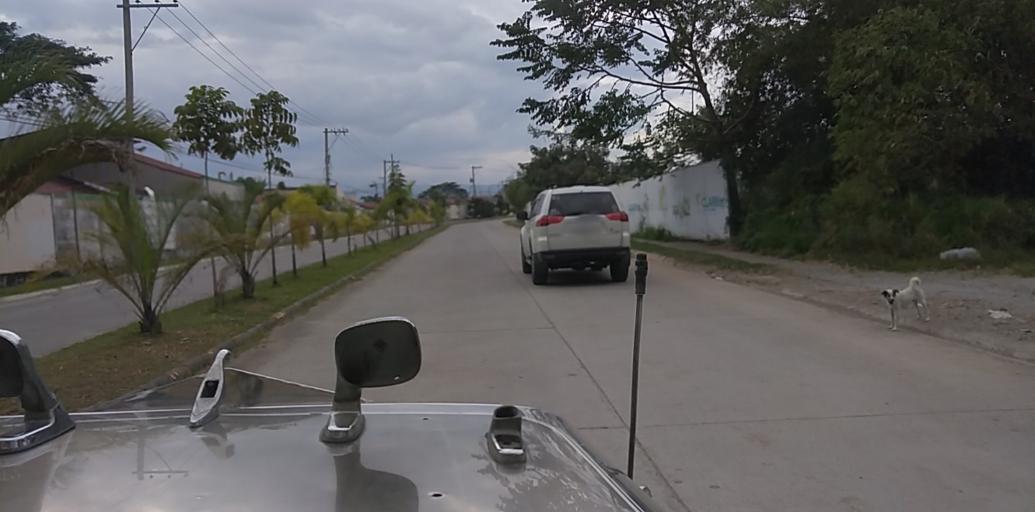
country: PH
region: Central Luzon
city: Santol
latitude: 15.1656
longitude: 120.5413
